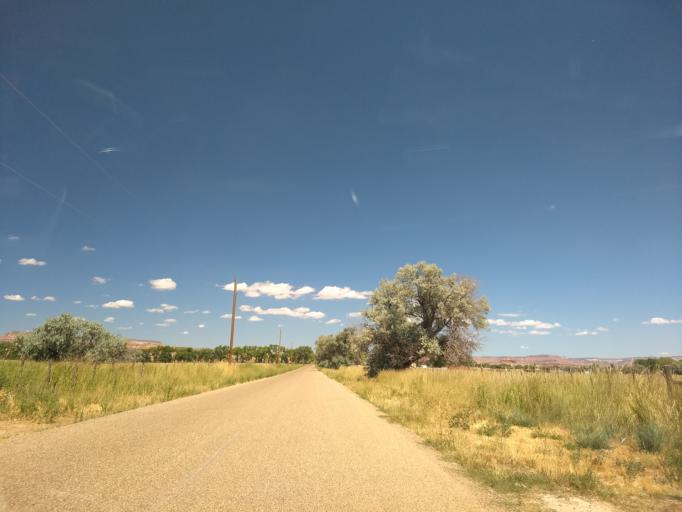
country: US
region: Arizona
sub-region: Coconino County
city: Fredonia
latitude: 36.9336
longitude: -112.5353
